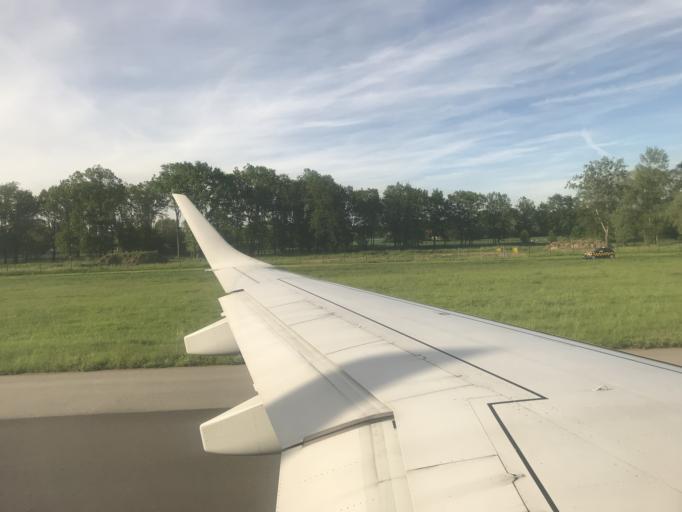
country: PL
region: Lower Silesian Voivodeship
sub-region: Powiat wroclawski
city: Smolec
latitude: 51.1051
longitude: 16.8892
